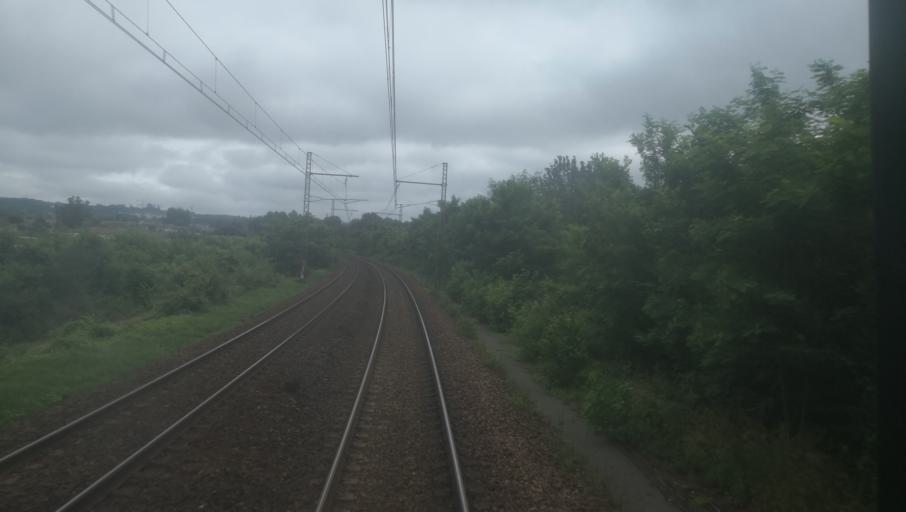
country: FR
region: Centre
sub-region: Departement du Cher
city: Vierzon
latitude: 47.2045
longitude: 2.1008
